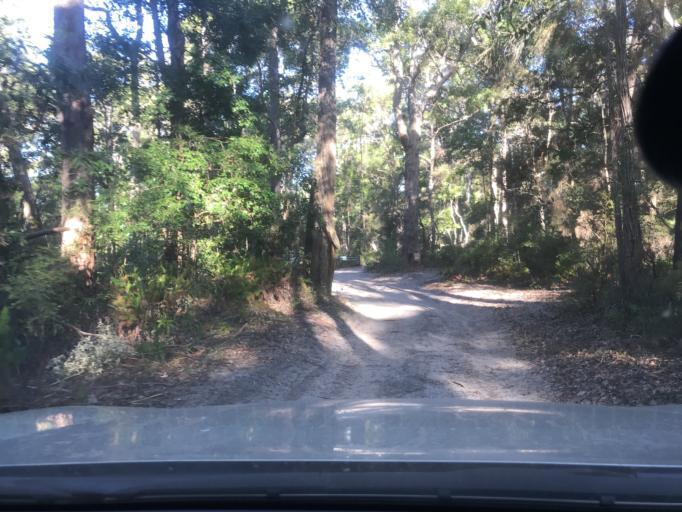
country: AU
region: Queensland
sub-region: Fraser Coast
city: Urangan
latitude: -25.3273
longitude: 153.1514
